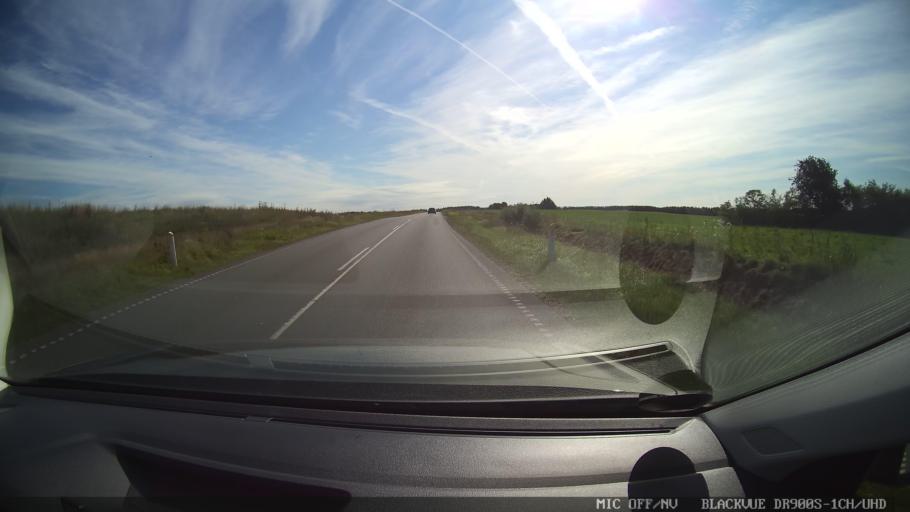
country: DK
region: North Denmark
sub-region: Mariagerfjord Kommune
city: Arden
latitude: 56.7648
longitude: 9.8987
